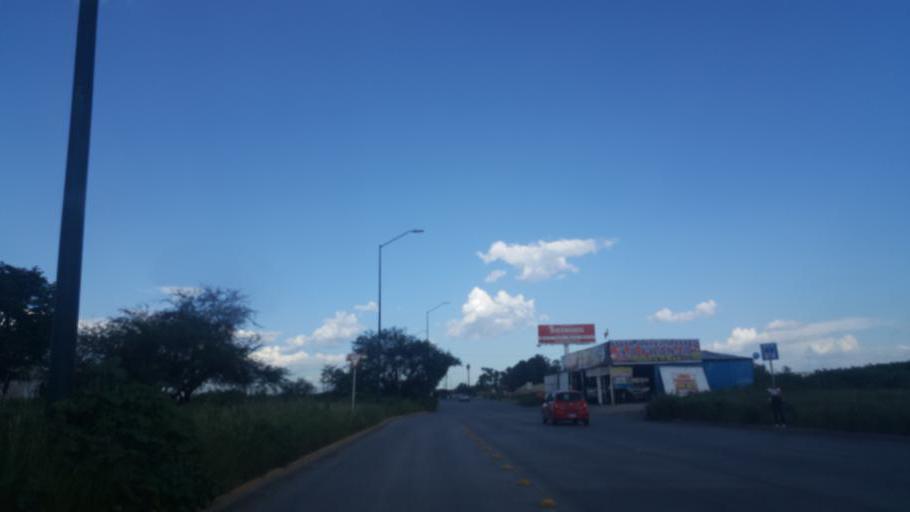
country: MX
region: Guanajuato
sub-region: Leon
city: San Jose de Duran (Los Troncoso)
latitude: 21.0962
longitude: -101.7021
